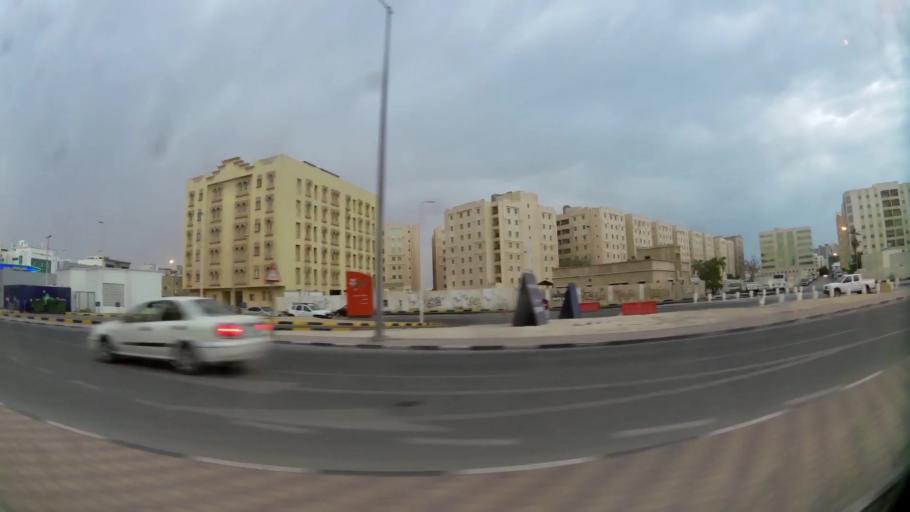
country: QA
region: Baladiyat ad Dawhah
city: Doha
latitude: 25.2718
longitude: 51.5203
